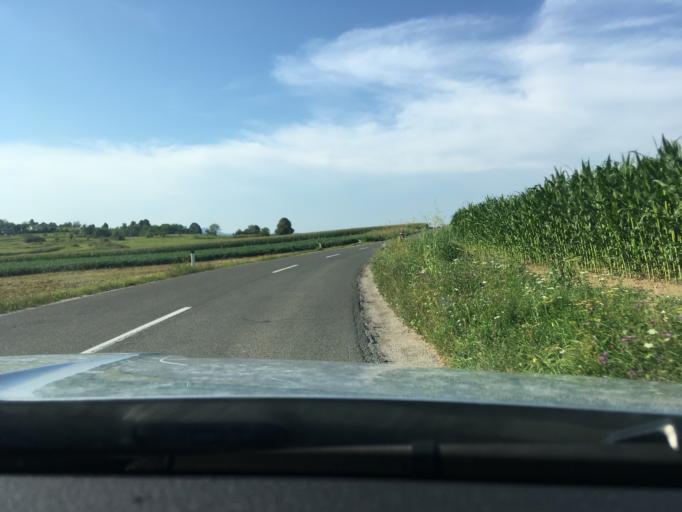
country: SI
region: Crnomelj
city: Crnomelj
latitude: 45.5275
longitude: 15.1629
